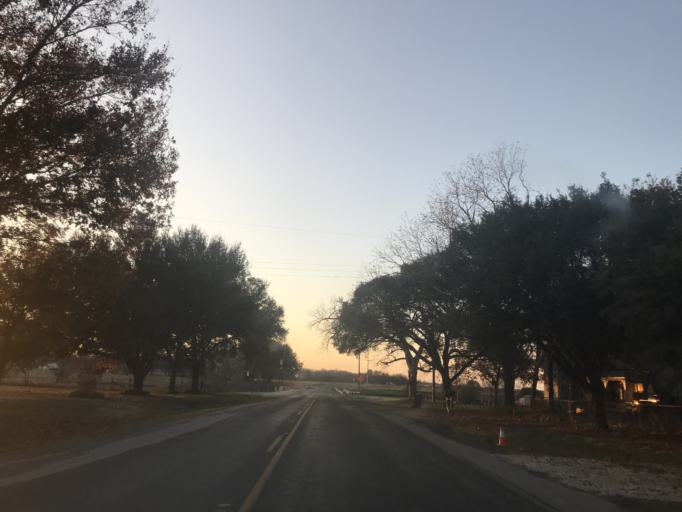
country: US
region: Texas
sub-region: Williamson County
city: Hutto
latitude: 30.4949
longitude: -97.4979
